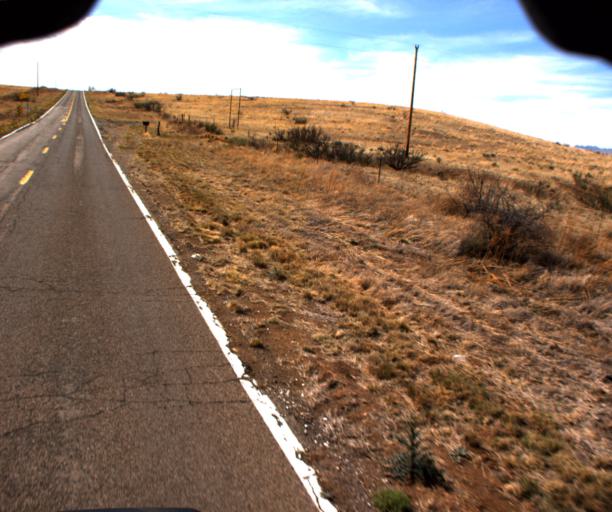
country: US
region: Arizona
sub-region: Cochise County
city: Willcox
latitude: 32.0068
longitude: -109.4240
